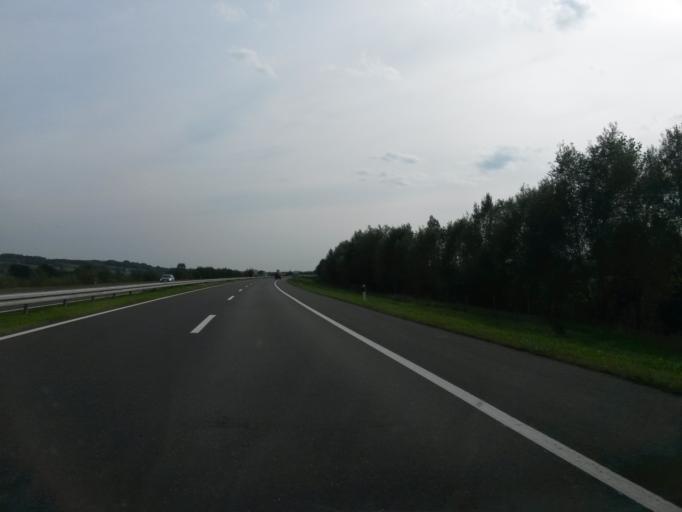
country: HR
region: Zagrebacka
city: Brckovljani
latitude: 46.0107
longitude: 16.2946
